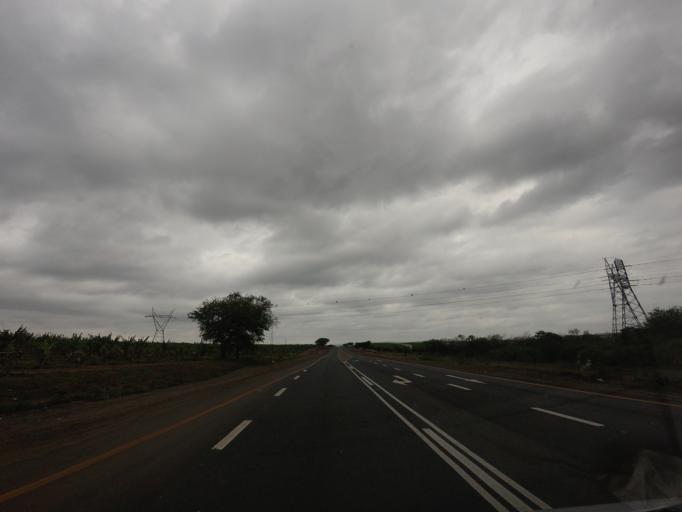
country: ZA
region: Mpumalanga
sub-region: Ehlanzeni District
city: Komatipoort
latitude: -25.4355
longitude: 31.8228
